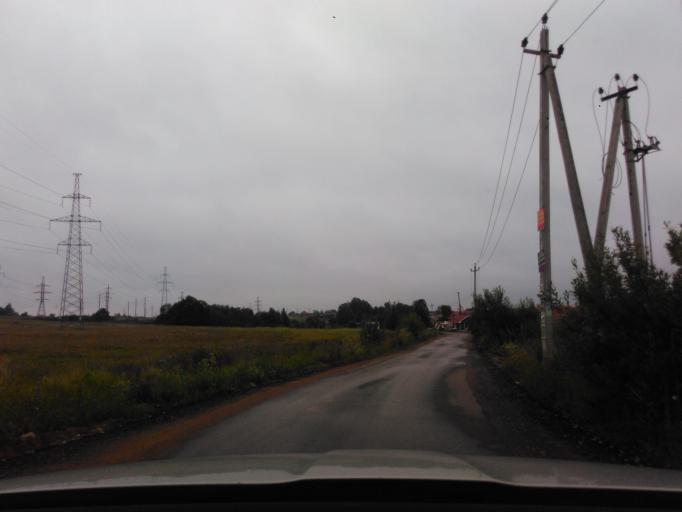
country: RU
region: Moskovskaya
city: Firsanovka
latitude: 55.9467
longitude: 37.2278
